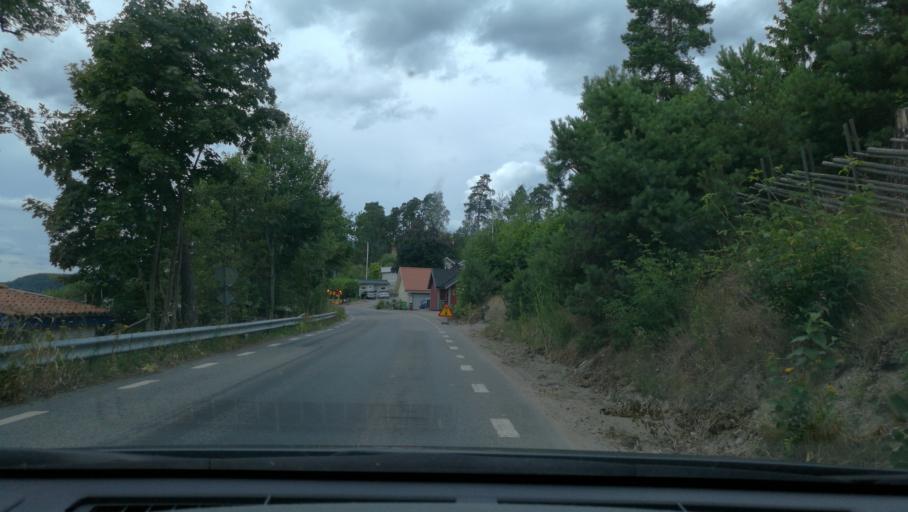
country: SE
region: OEstergoetland
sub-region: Norrkopings Kommun
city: Krokek
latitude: 58.6633
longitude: 16.3660
